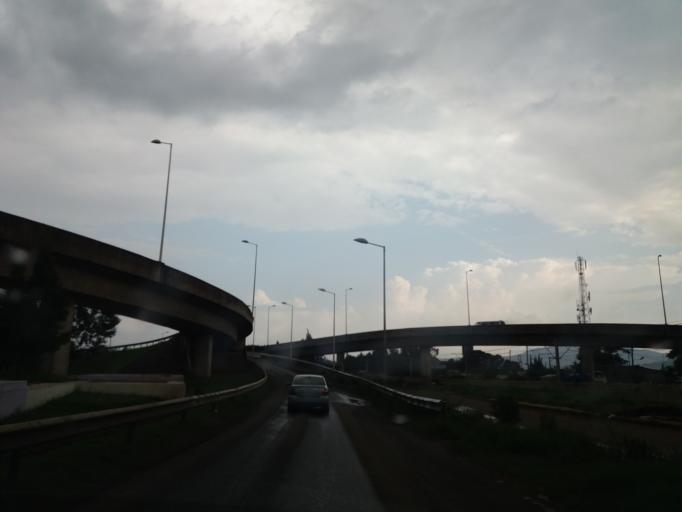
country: ET
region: Adis Abeba
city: Addis Ababa
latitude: 8.9809
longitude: 38.7593
